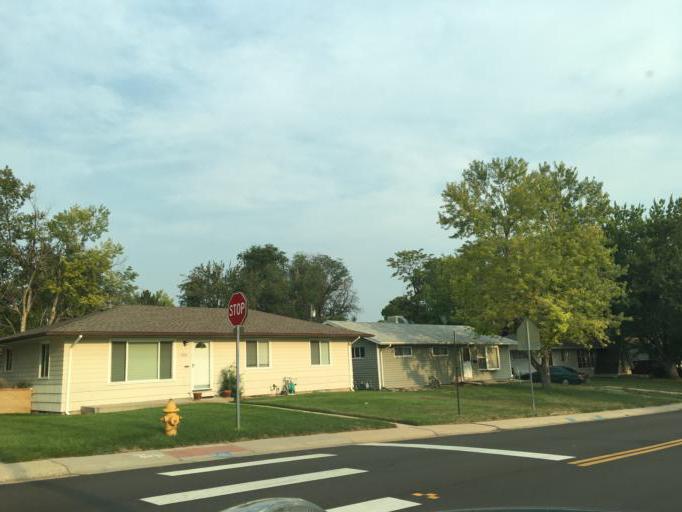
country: US
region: Colorado
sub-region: Arapahoe County
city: Glendale
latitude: 39.6875
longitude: -104.9318
